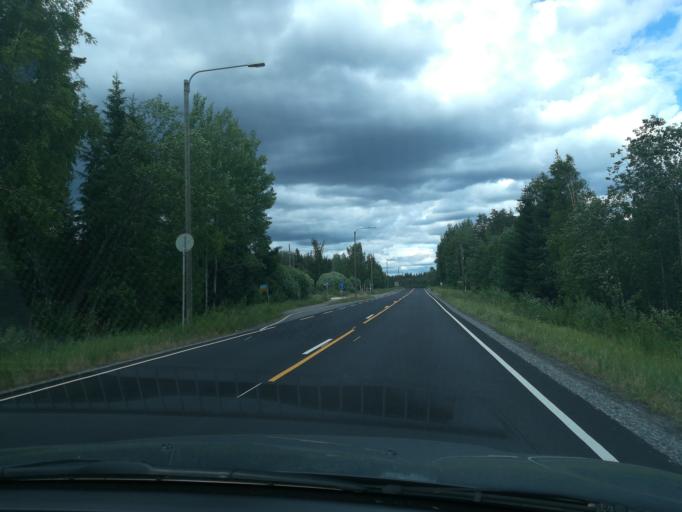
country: FI
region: Southern Savonia
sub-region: Mikkeli
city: Mikkeli
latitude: 61.6567
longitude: 27.1008
